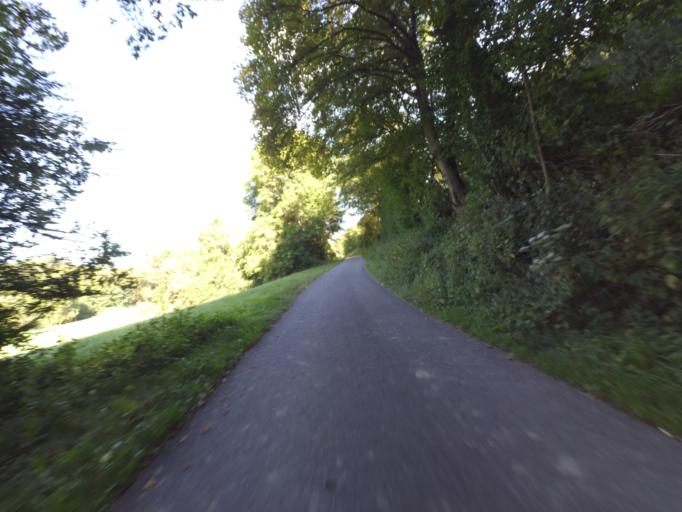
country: DE
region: Rheinland-Pfalz
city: Daun
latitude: 50.1878
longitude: 6.8176
